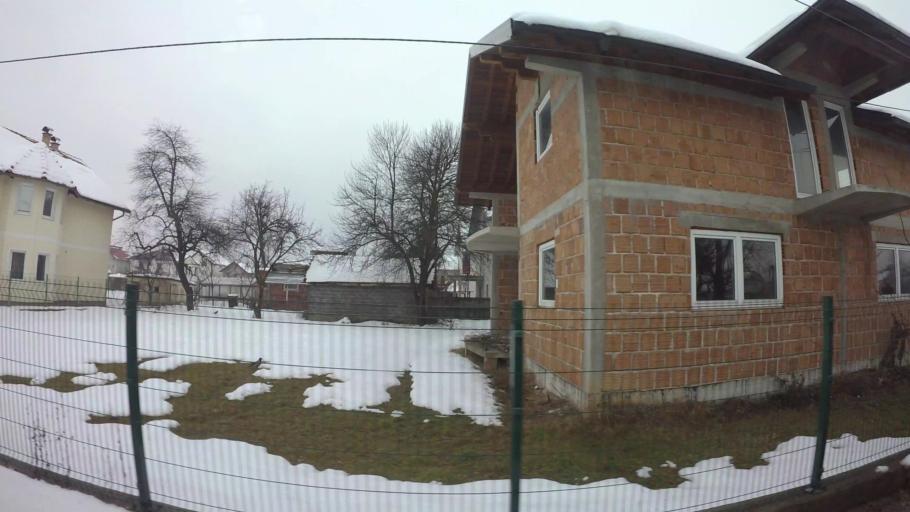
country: BA
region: Federation of Bosnia and Herzegovina
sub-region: Kanton Sarajevo
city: Sarajevo
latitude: 43.8385
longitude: 18.2819
